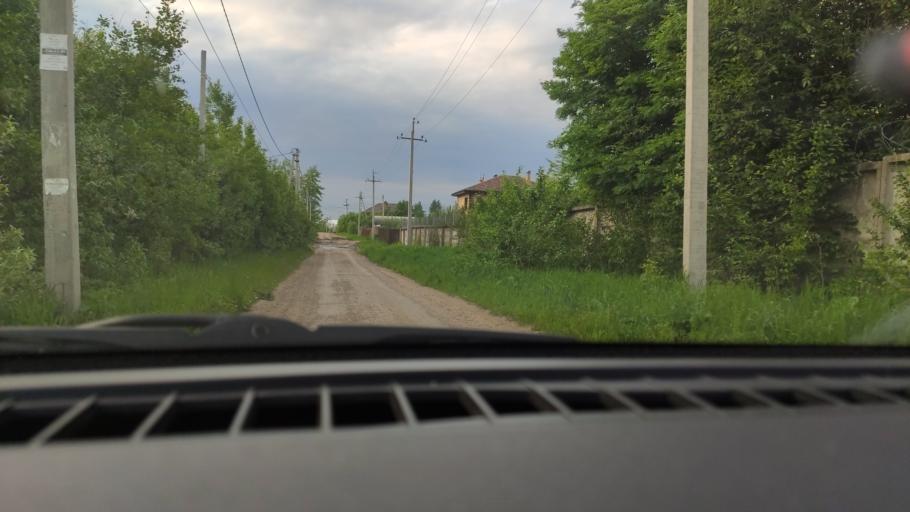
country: RU
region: Perm
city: Froly
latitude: 57.9510
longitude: 56.2848
